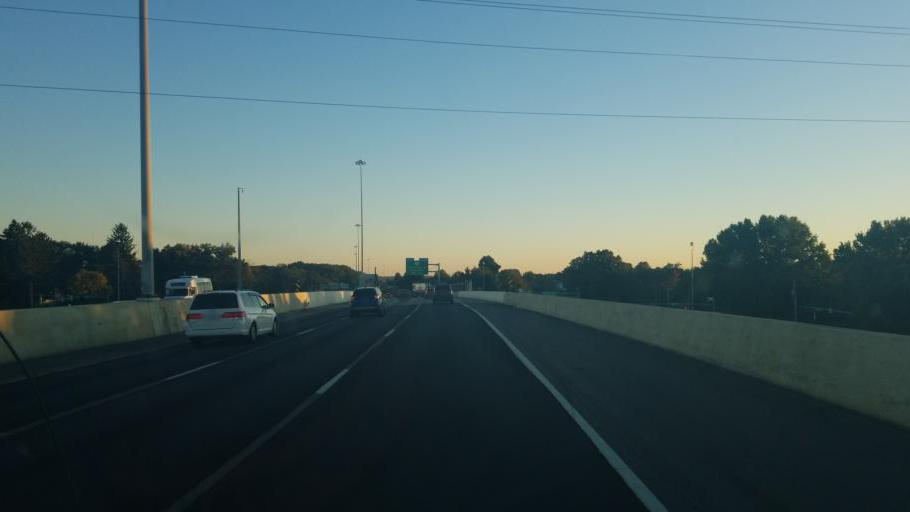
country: US
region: Ohio
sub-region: Stark County
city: Canton
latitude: 40.8123
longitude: -81.3978
